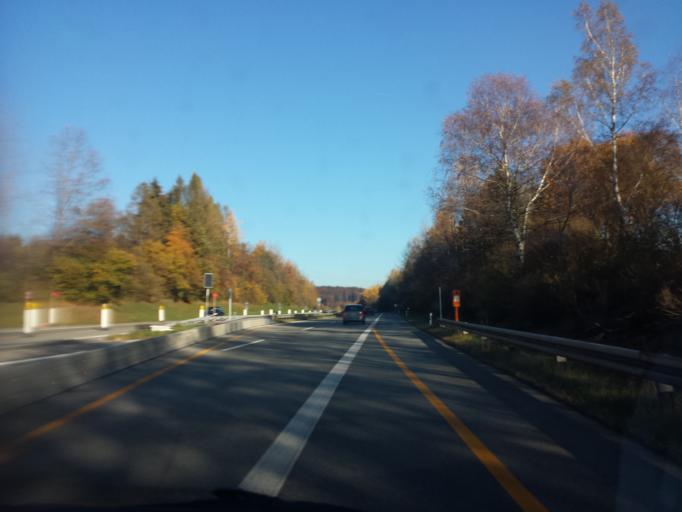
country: DE
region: Bavaria
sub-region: Upper Bavaria
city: Ohlstadt
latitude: 47.6633
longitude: 11.2512
